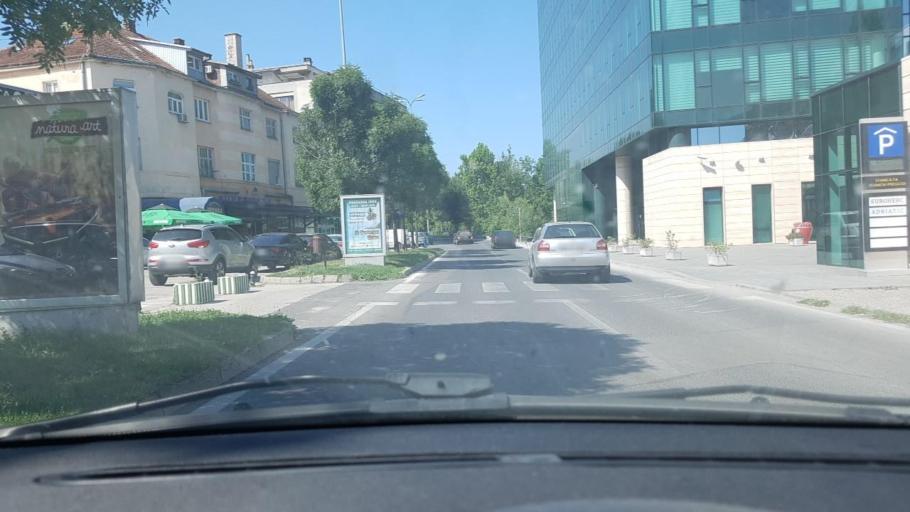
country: BA
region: Federation of Bosnia and Herzegovina
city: Bihac
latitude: 44.8154
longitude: 15.8705
